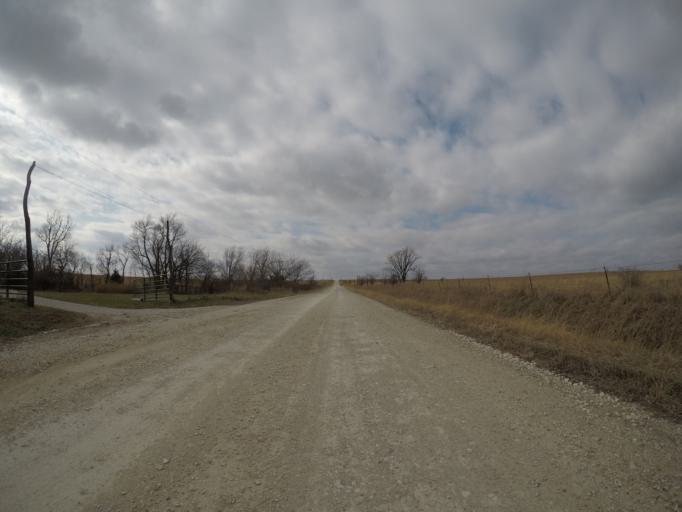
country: US
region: Kansas
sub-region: Morris County
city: Council Grove
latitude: 38.7682
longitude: -96.3359
